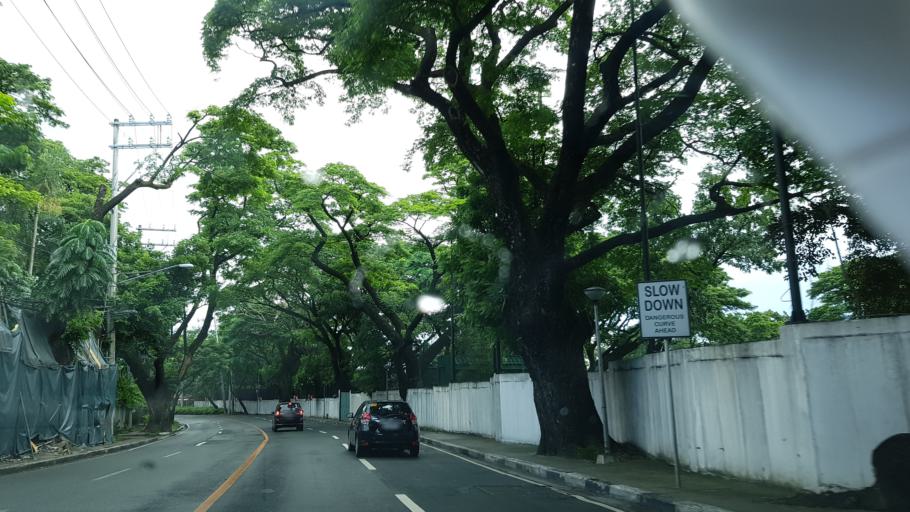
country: PH
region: Metro Manila
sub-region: Makati City
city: Makati City
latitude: 14.5468
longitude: 121.0415
